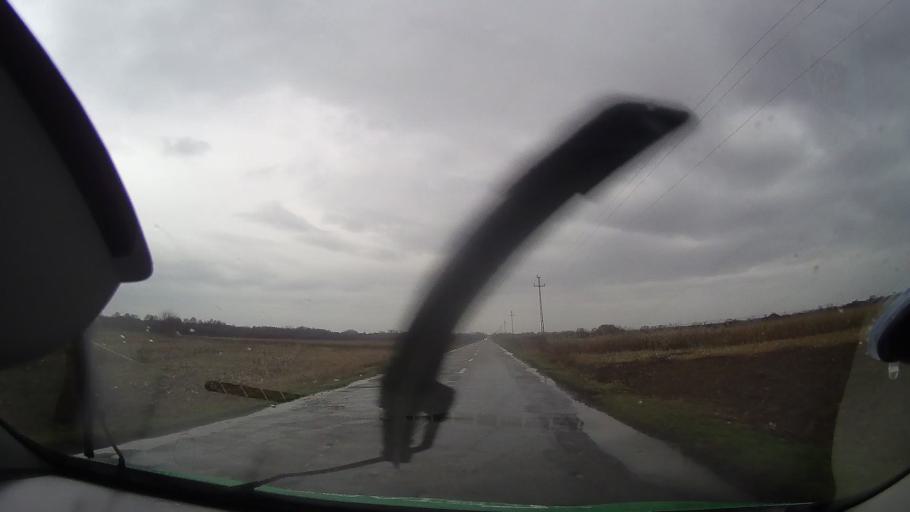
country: RO
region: Bihor
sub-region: Comuna Soimi
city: Soimi
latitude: 46.6881
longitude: 22.1055
